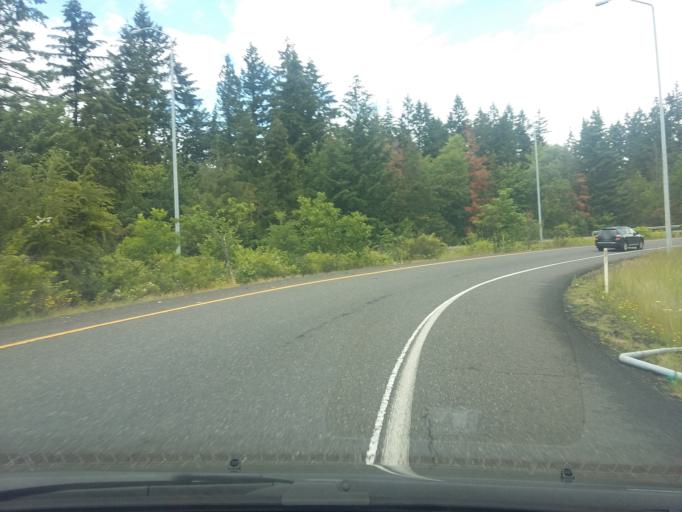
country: US
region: Washington
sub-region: Clark County
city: Barberton
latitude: 45.6844
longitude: -122.5938
